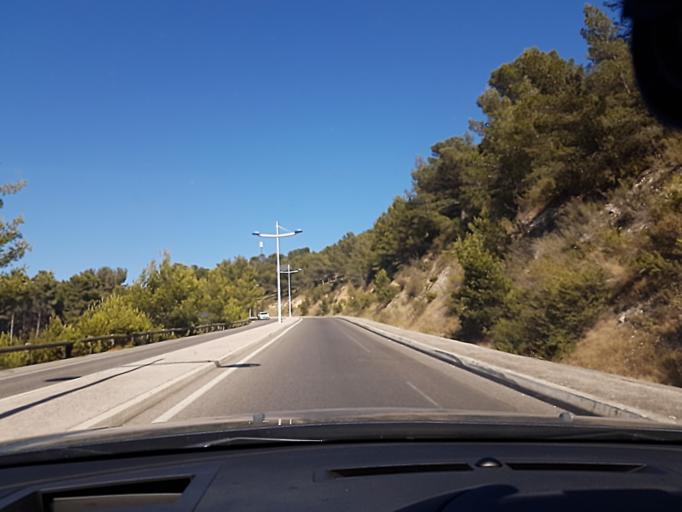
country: FR
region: Provence-Alpes-Cote d'Azur
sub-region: Departement des Bouches-du-Rhone
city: Carry-le-Rouet
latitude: 43.3382
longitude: 5.1601
